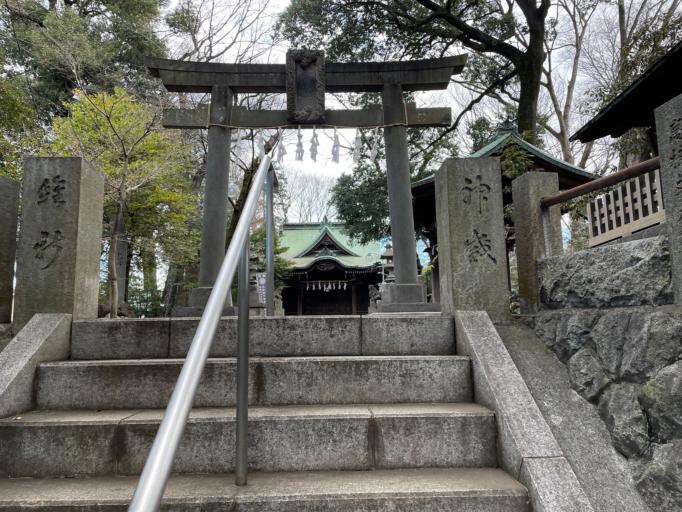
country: JP
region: Tokyo
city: Chofugaoka
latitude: 35.6531
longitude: 139.5284
